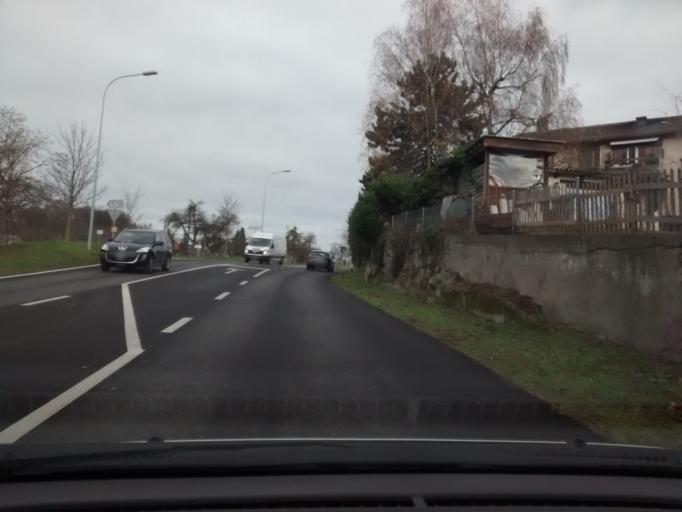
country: CH
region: Vaud
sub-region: Lausanne District
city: Blecherette
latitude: 46.5449
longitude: 6.6102
